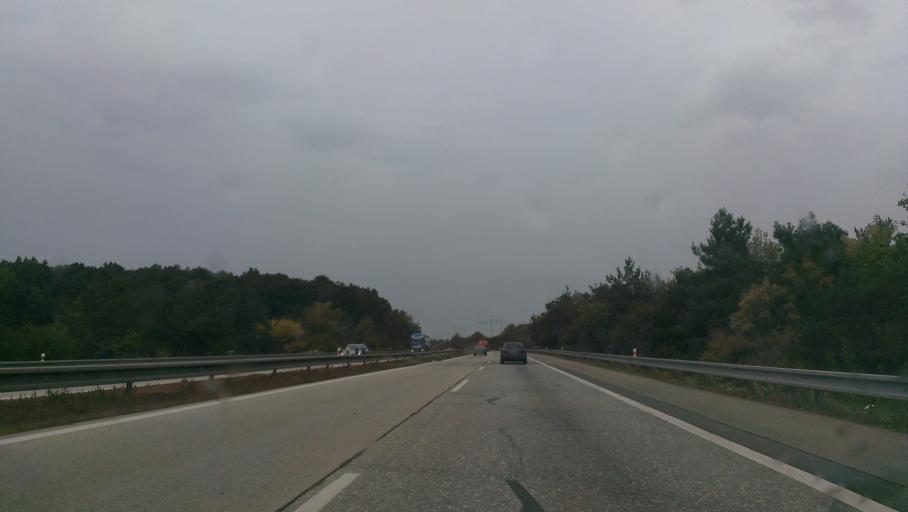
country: CZ
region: South Moravian
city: Ricany
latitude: 49.2410
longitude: 16.3697
